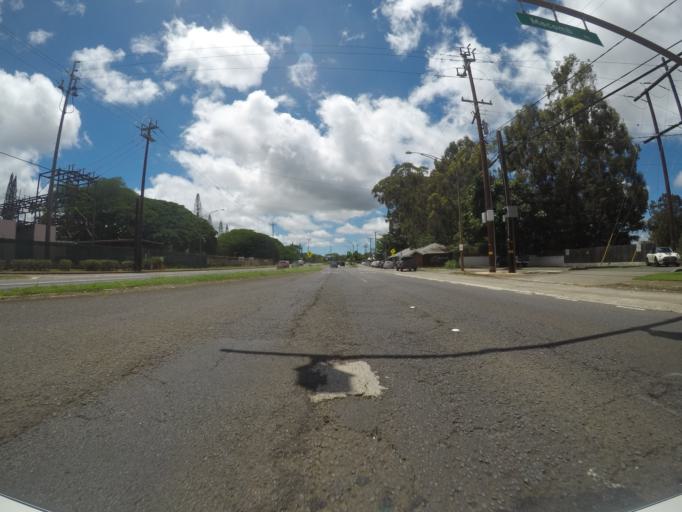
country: US
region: Hawaii
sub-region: Honolulu County
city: Schofield Barracks
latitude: 21.4937
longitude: -158.0490
